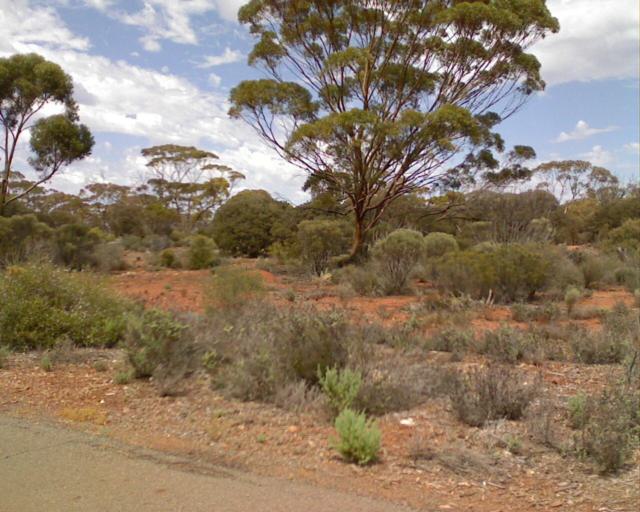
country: AU
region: Western Australia
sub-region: Kalgoorlie/Boulder
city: Stoneville
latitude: -31.2112
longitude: 121.6238
